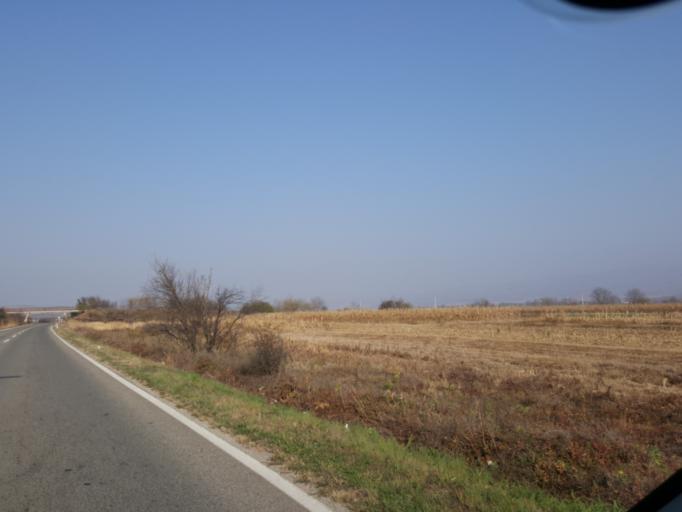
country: RS
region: Central Serbia
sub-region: Jablanicki Okrug
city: Leskovac
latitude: 43.0311
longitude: 21.9426
